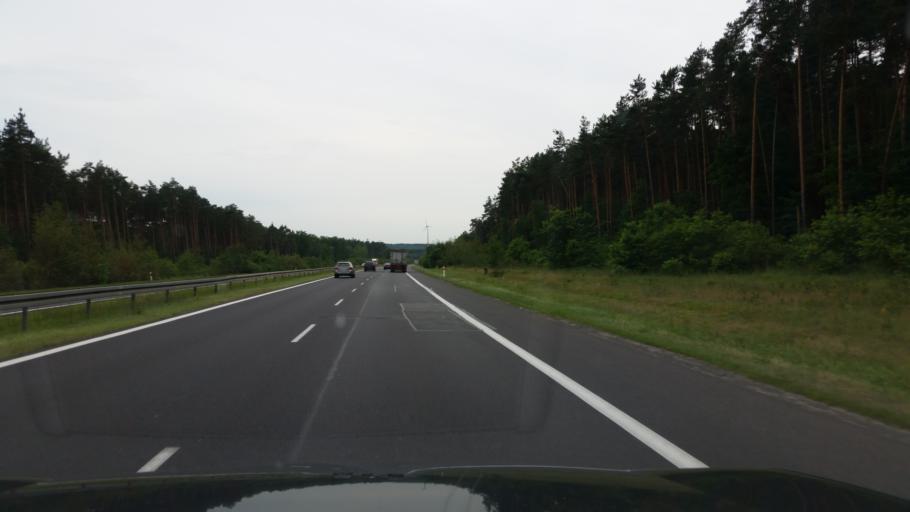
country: PL
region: Lodz Voivodeship
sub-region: Powiat radomszczanski
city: Gomunice
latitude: 51.1649
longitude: 19.4569
